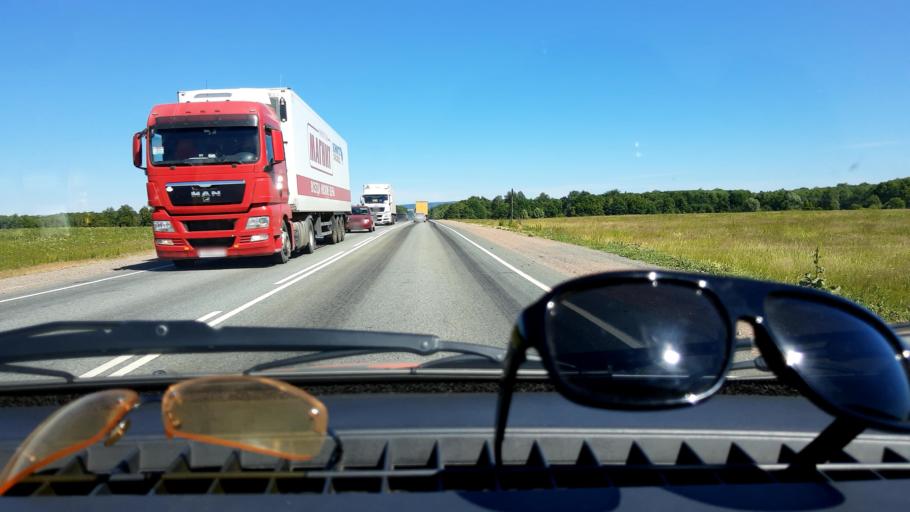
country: RU
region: Bashkortostan
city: Kudeyevskiy
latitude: 54.8173
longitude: 56.8171
